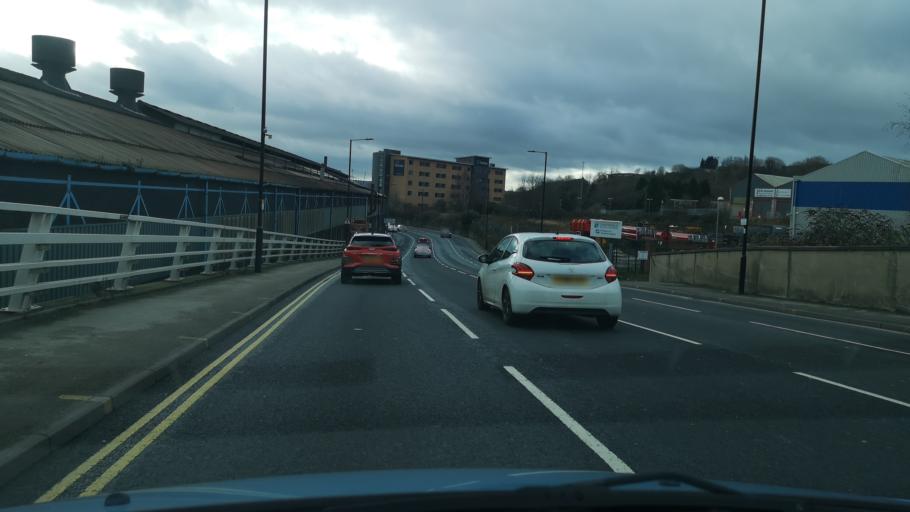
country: GB
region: England
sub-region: Rotherham
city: Wentworth
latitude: 53.4209
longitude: -1.4119
